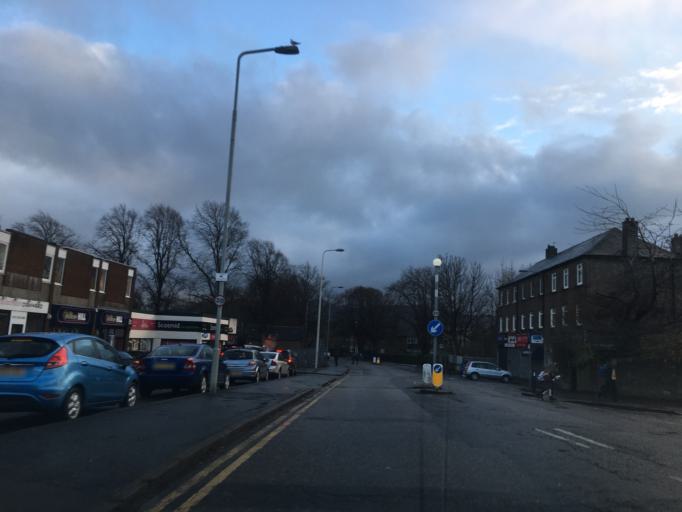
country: GB
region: Scotland
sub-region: Edinburgh
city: Colinton
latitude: 55.9367
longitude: -3.2793
